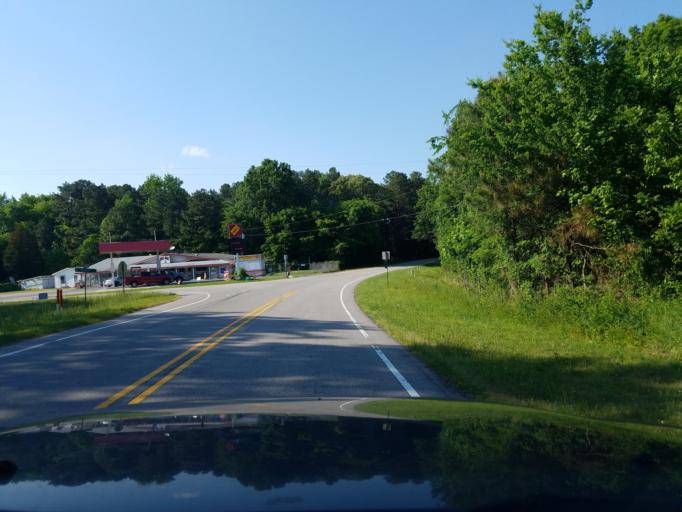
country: US
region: North Carolina
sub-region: Vance County
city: Henderson
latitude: 36.4062
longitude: -78.3691
